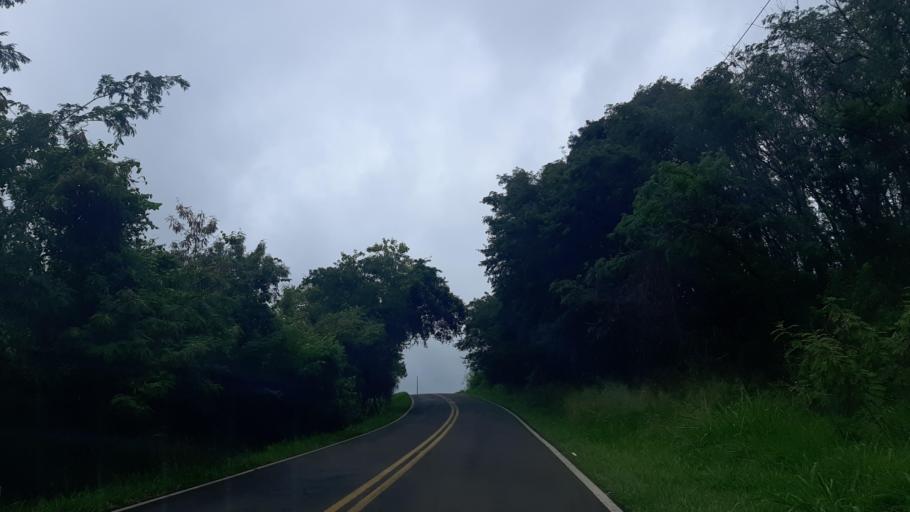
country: BR
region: Parana
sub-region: Ampere
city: Ampere
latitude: -25.9862
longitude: -53.4416
